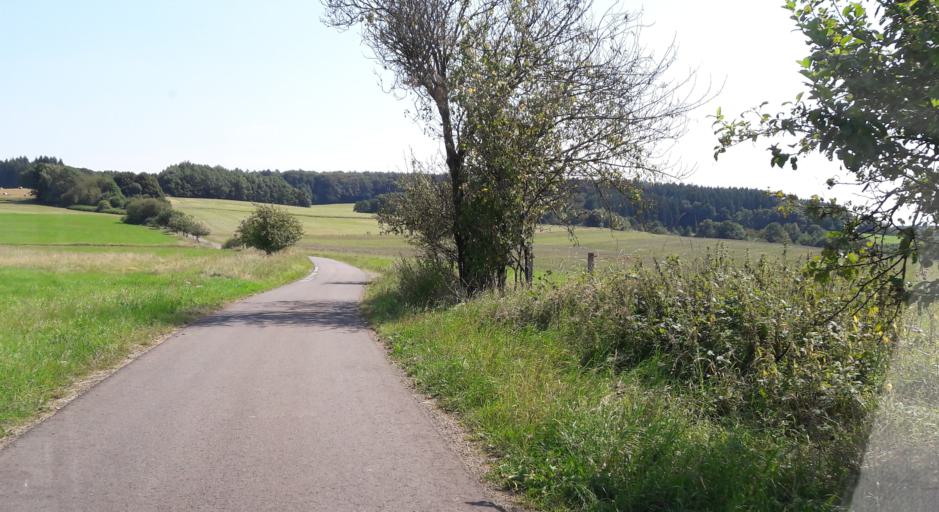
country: DE
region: Saarland
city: Mainzweiler
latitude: 49.4103
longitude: 7.1101
